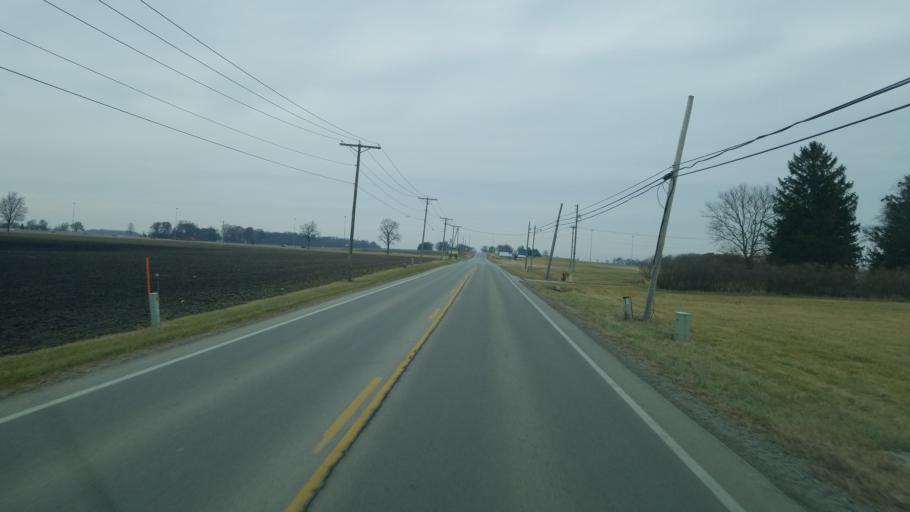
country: US
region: Ohio
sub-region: Wyandot County
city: Upper Sandusky
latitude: 40.8511
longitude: -83.2798
